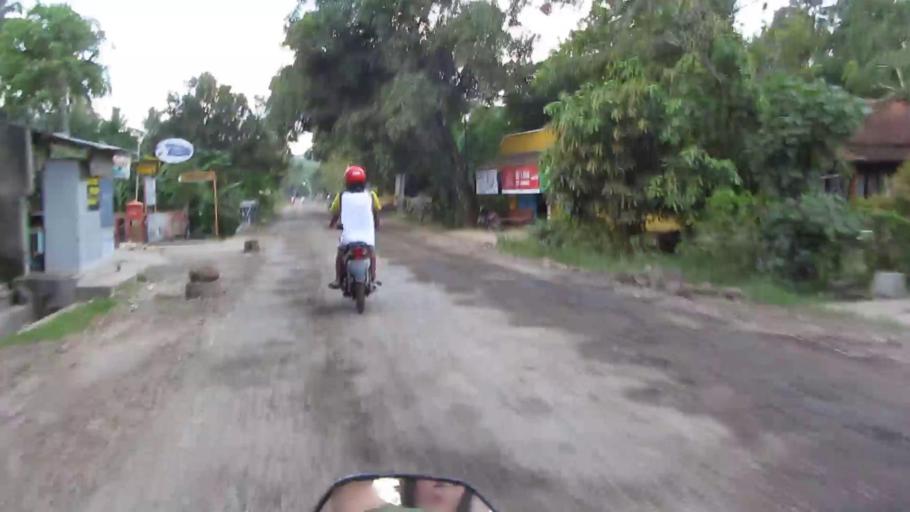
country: ID
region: West Java
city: Binangun
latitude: -7.7166
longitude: 108.4765
